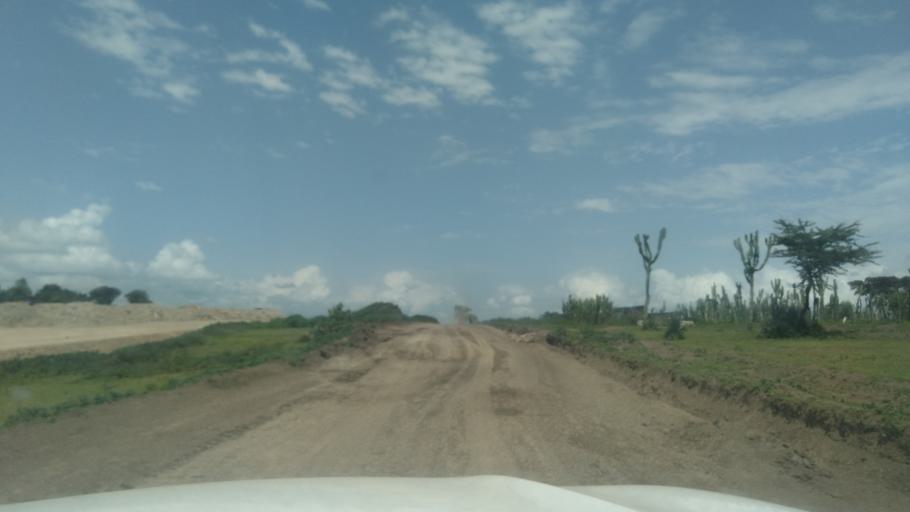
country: ET
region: Oromiya
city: Shashemene
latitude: 7.2775
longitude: 38.6033
